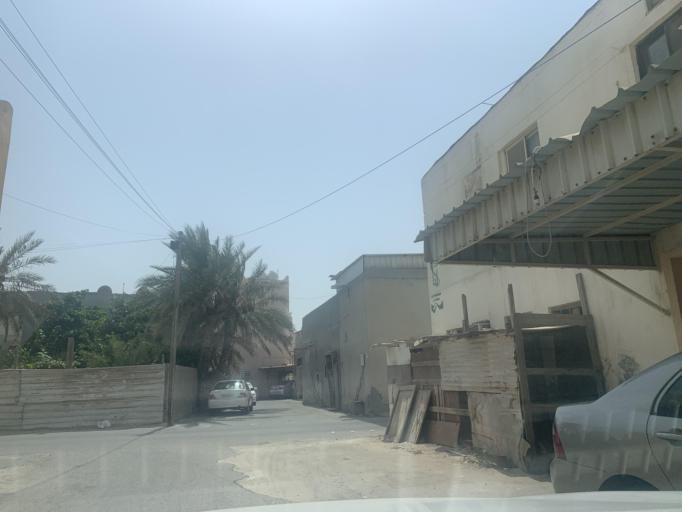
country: BH
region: Manama
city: Jidd Hafs
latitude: 26.2216
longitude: 50.4672
